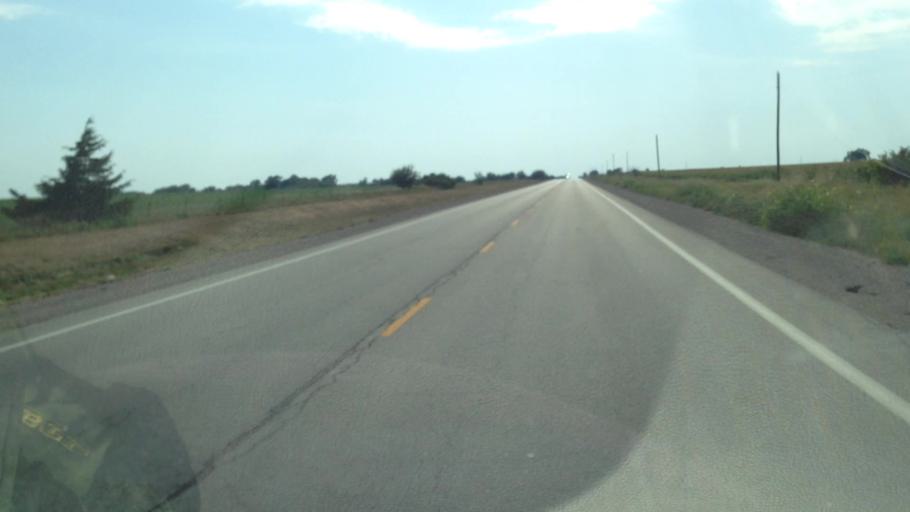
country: US
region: Kansas
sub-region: Anderson County
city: Garnett
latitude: 38.0816
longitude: -95.2067
